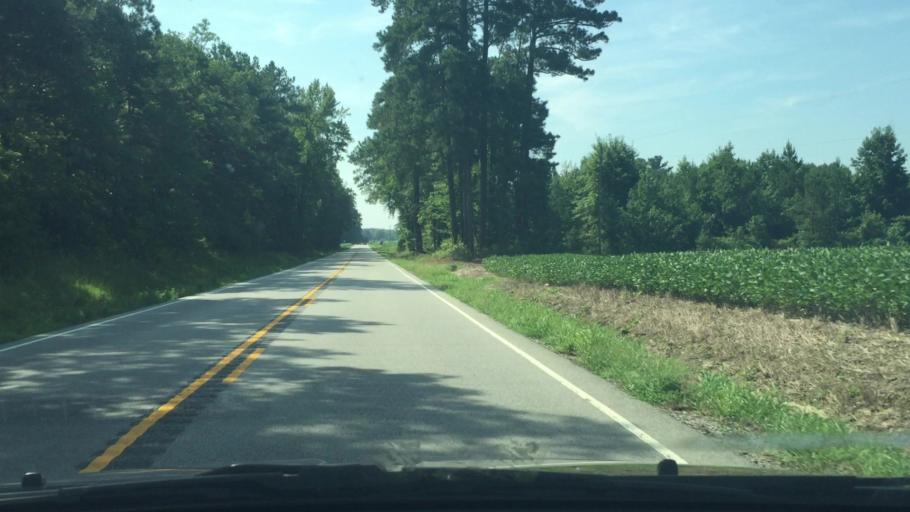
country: US
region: Virginia
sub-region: Southampton County
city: Courtland
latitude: 36.8552
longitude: -77.1351
